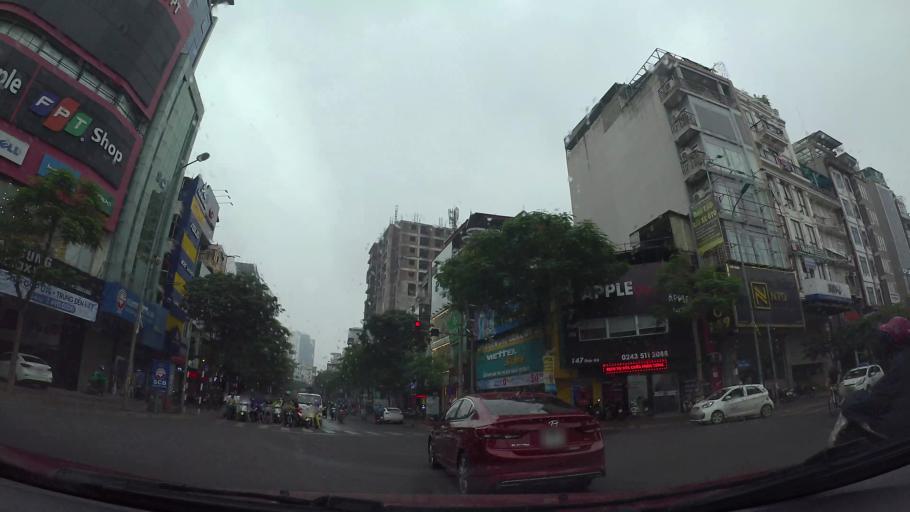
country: VN
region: Ha Noi
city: Dong Da
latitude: 21.0139
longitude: 105.8189
